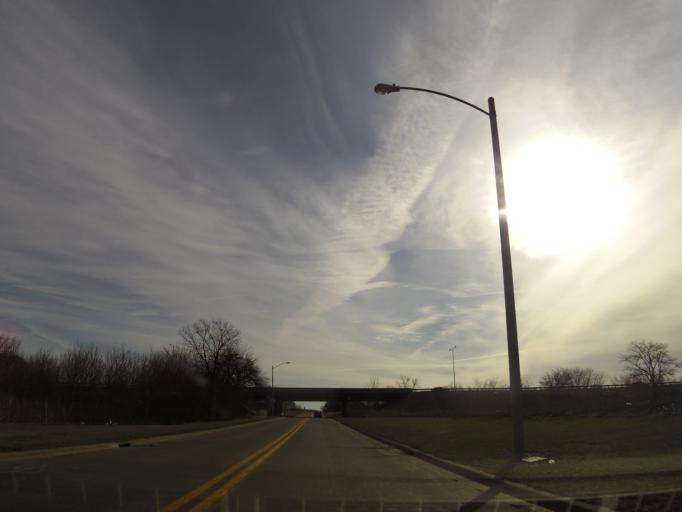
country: US
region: Illinois
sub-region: McLean County
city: Normal
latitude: 40.5096
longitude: -89.0304
